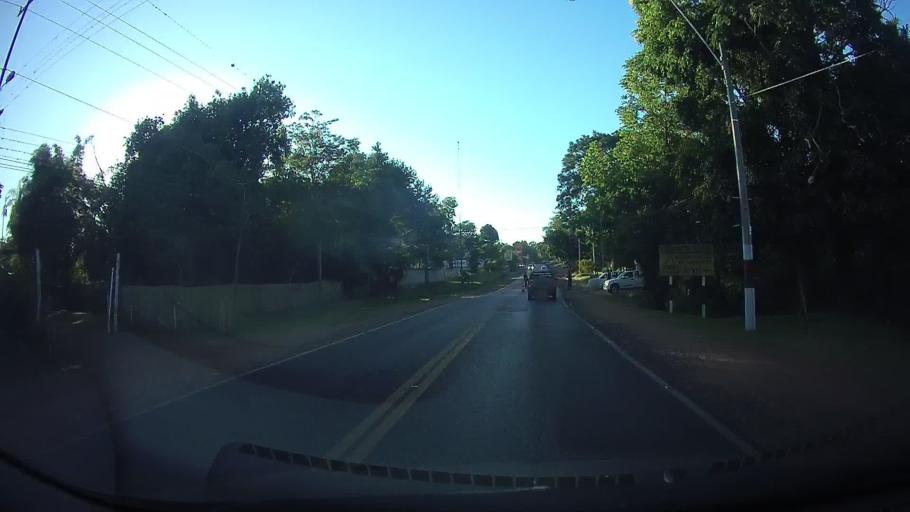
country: PY
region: Central
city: Aregua
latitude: -25.3043
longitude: -57.3996
